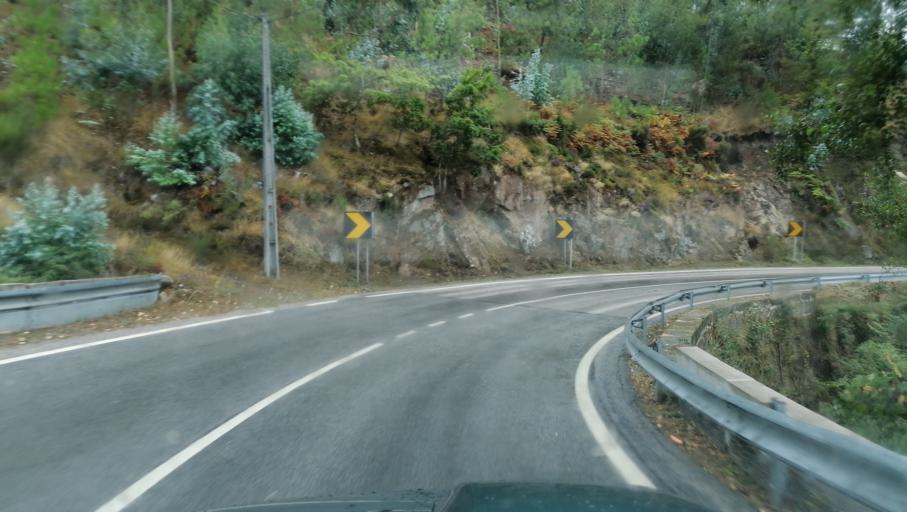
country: PT
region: Vila Real
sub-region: Ribeira de Pena
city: Ribeira de Pena
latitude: 41.5213
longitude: -7.8318
